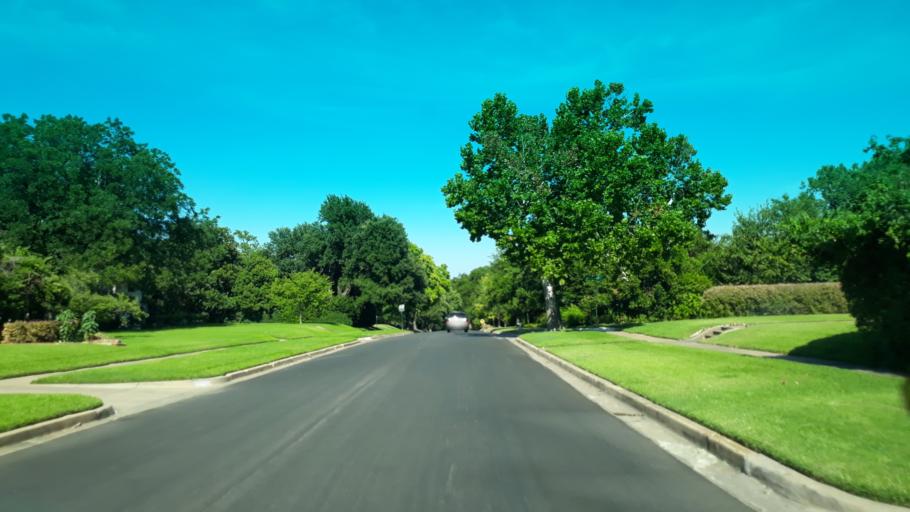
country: US
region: Texas
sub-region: Dallas County
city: Highland Park
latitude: 32.8195
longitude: -96.7444
